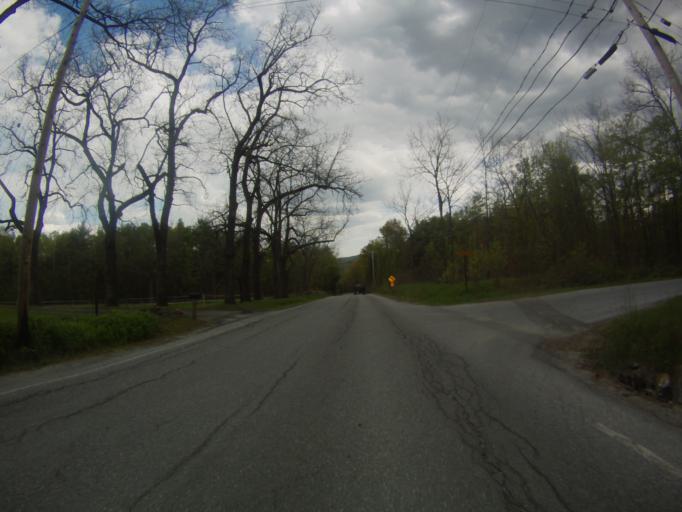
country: US
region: New York
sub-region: Essex County
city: Mineville
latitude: 44.0776
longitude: -73.5277
